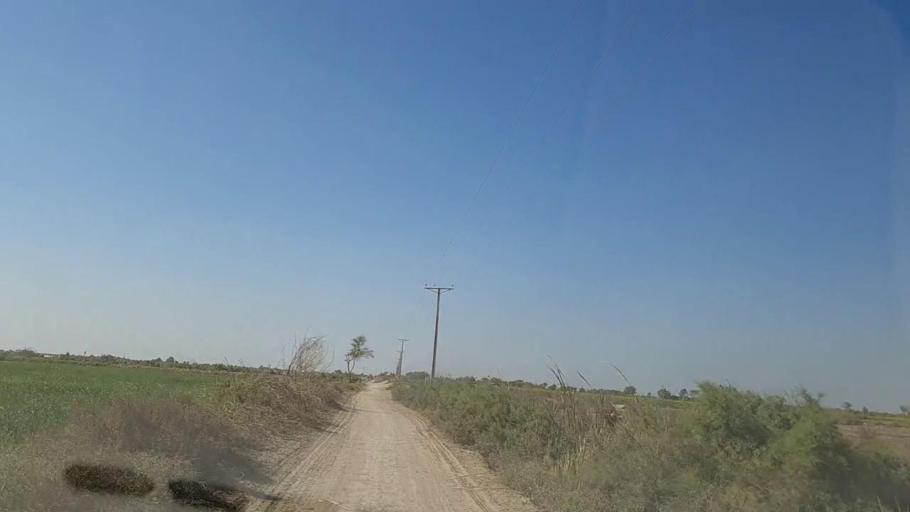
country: PK
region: Sindh
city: Digri
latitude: 25.1272
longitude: 69.0638
